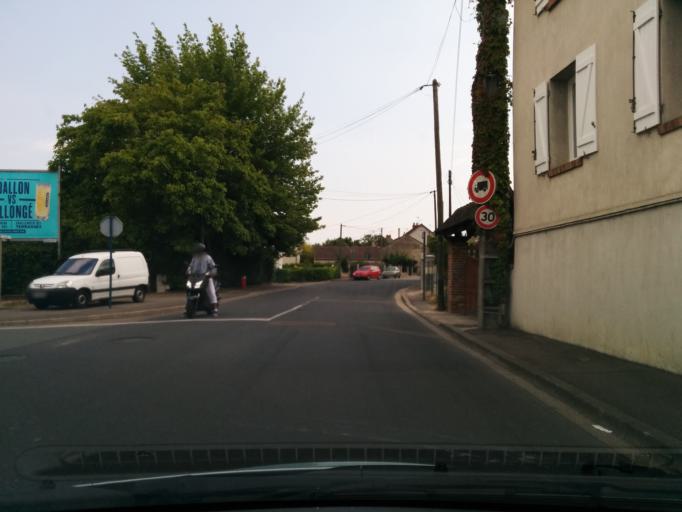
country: FR
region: Ile-de-France
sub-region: Departement des Yvelines
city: Mantes-la-Jolie
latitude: 48.9966
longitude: 1.7079
